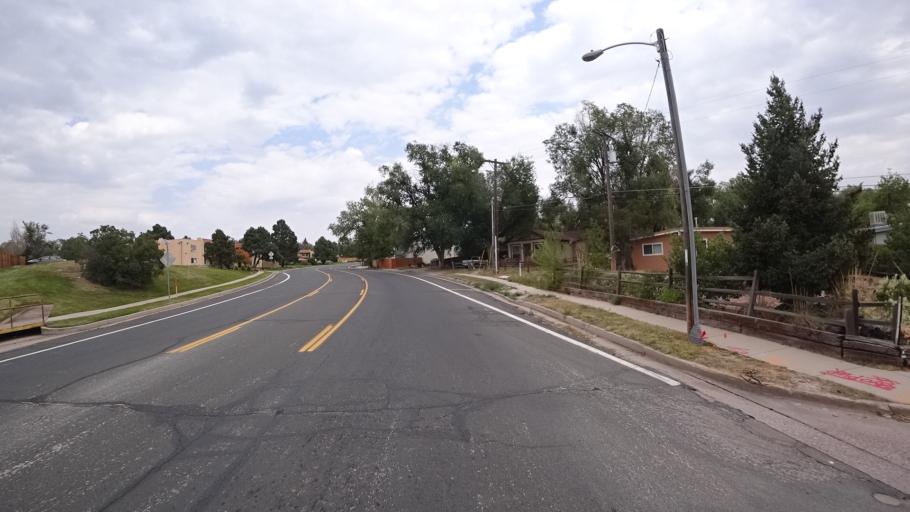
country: US
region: Colorado
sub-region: El Paso County
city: Colorado Springs
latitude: 38.8452
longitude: -104.7826
